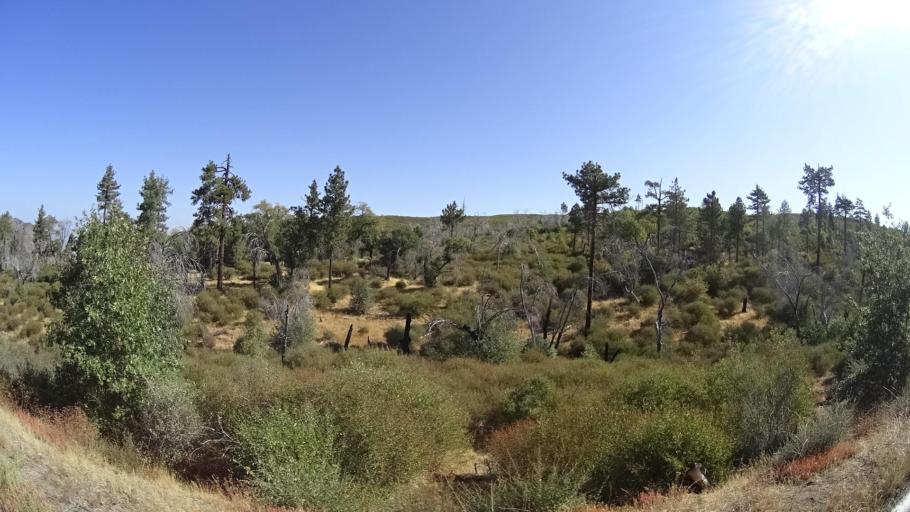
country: US
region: California
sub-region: San Diego County
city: Pine Valley
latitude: 32.8919
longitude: -116.4457
